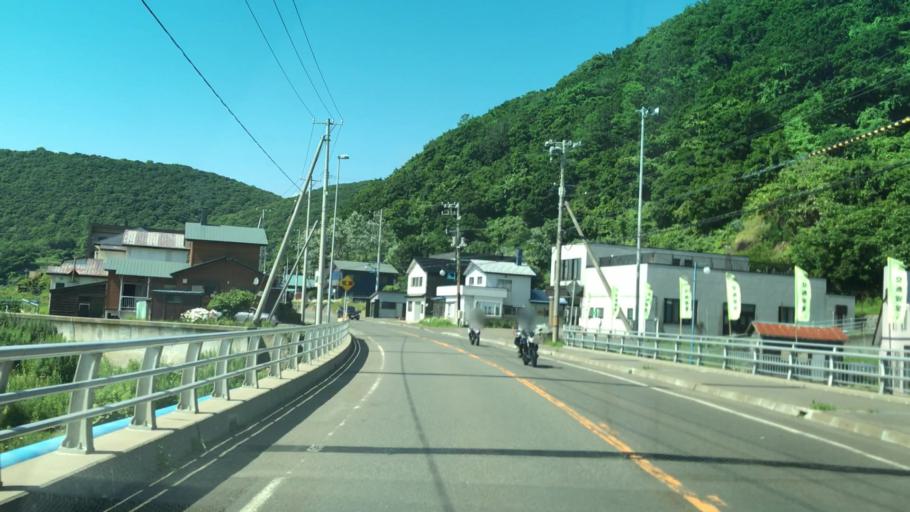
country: JP
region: Hokkaido
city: Iwanai
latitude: 43.1008
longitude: 140.4612
